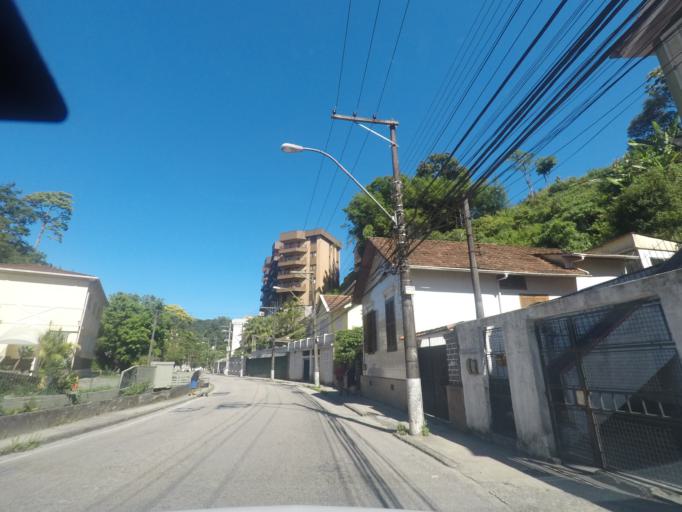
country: BR
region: Rio de Janeiro
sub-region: Petropolis
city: Petropolis
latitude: -22.5216
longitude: -43.1853
